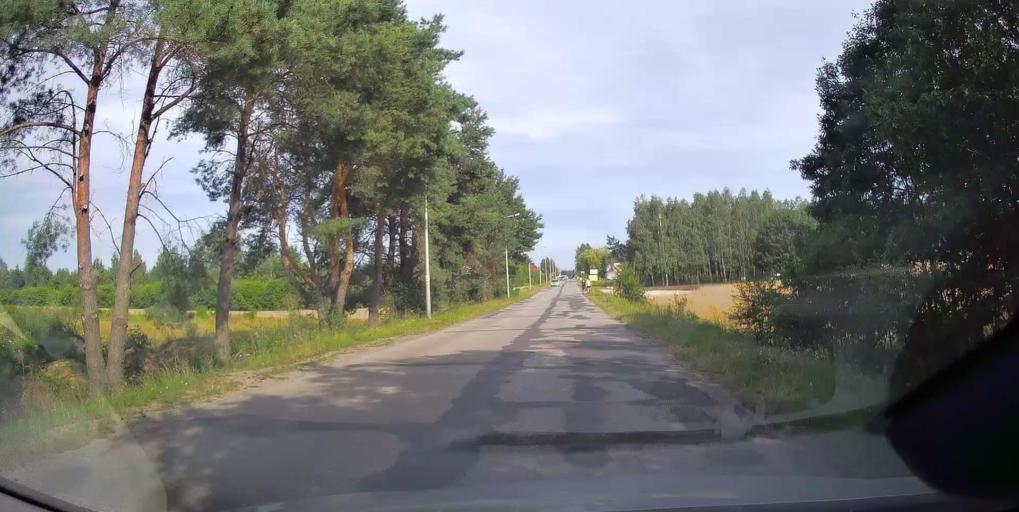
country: PL
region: Lodz Voivodeship
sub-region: Powiat tomaszowski
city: Tomaszow Mazowiecki
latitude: 51.4706
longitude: 20.0178
